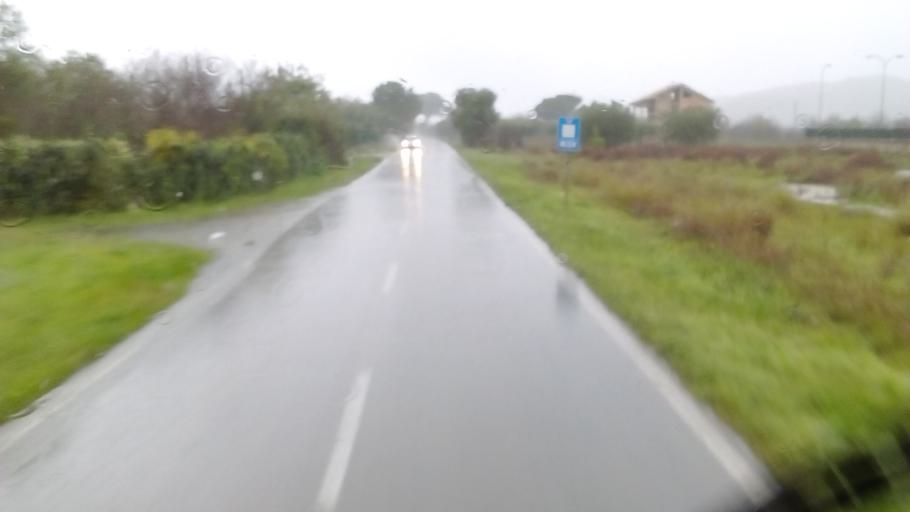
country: IT
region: Sicily
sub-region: Enna
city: Pietraperzia
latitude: 37.4200
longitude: 14.1697
